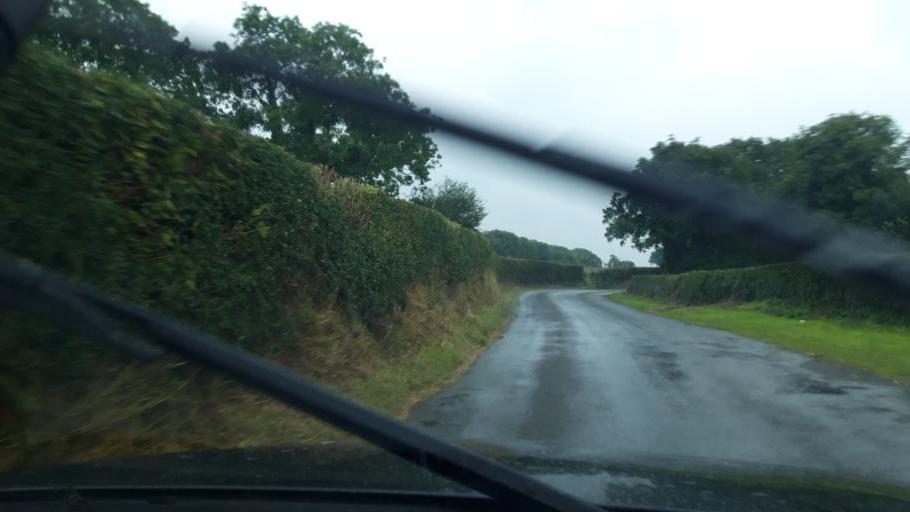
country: IE
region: Leinster
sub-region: Kilkenny
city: Callan
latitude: 52.6596
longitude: -7.4353
